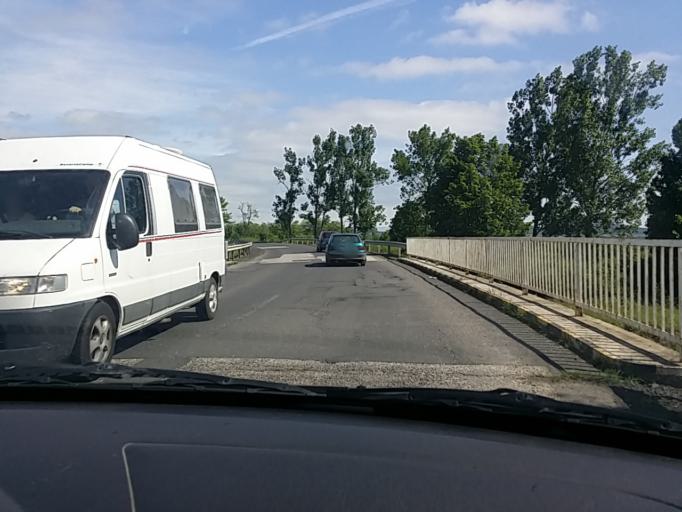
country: HU
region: Borsod-Abauj-Zemplen
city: Satoraljaujhely
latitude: 48.4434
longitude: 21.6256
